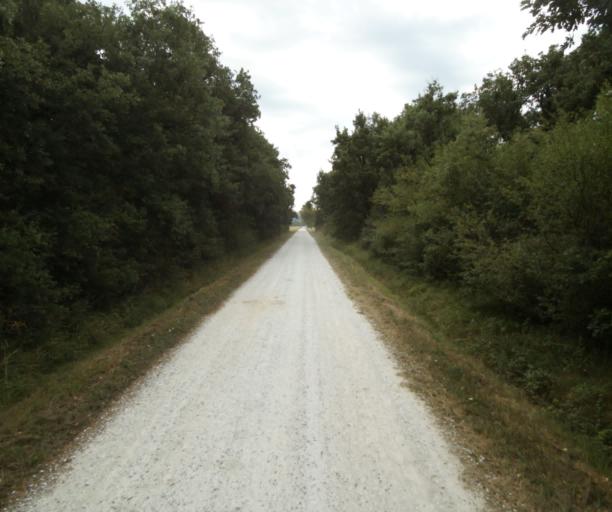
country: FR
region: Midi-Pyrenees
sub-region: Departement de la Haute-Garonne
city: Saint-Felix-Lauragais
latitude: 43.4404
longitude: 1.9389
